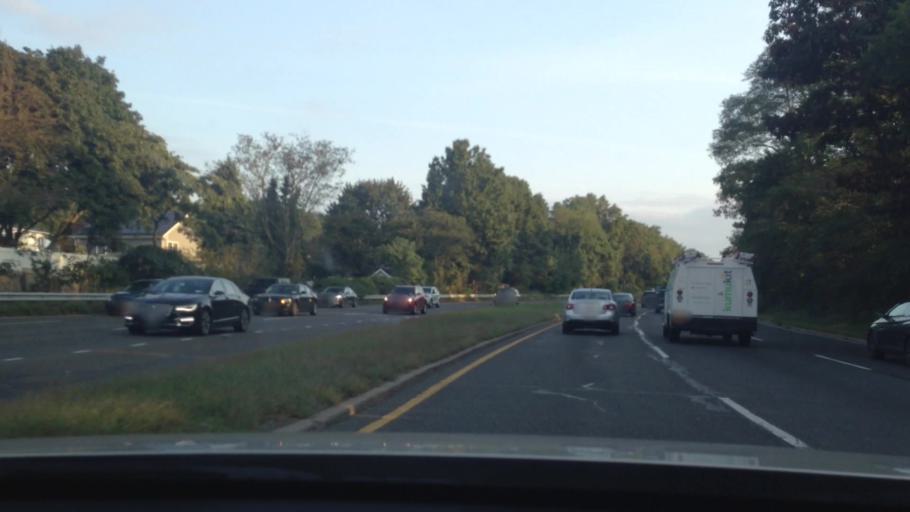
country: US
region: New York
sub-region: Suffolk County
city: Farmingville
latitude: 40.8355
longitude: -73.0213
